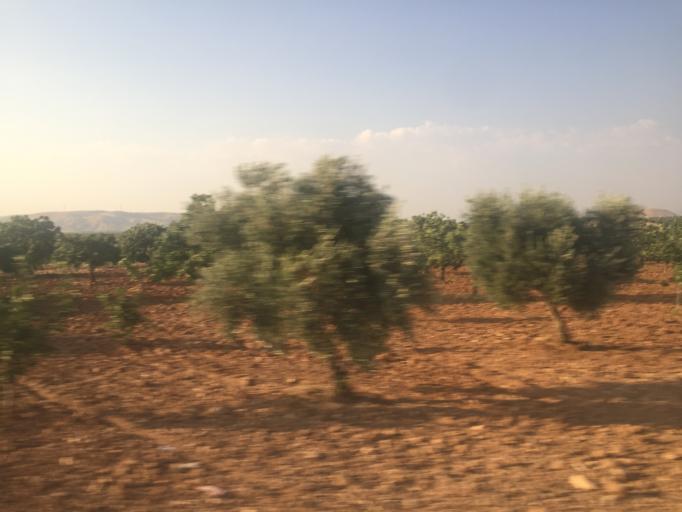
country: TR
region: Gaziantep
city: Nizip
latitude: 37.0142
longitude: 37.8393
